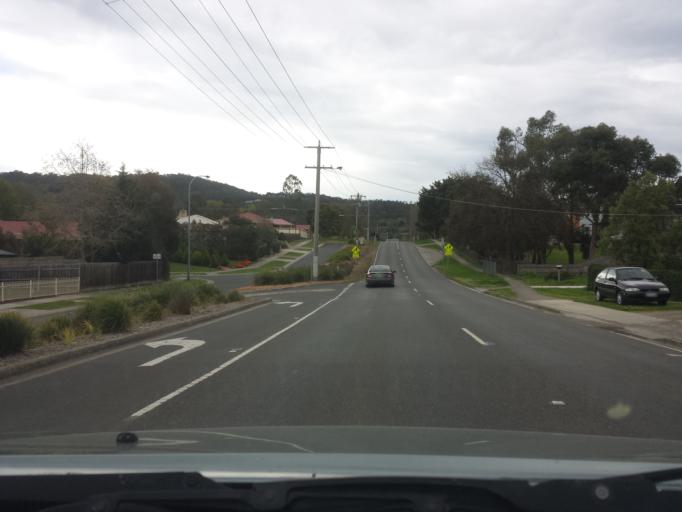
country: AU
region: Victoria
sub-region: Yarra Ranges
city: Yarra Glen
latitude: -37.6507
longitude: 145.3736
